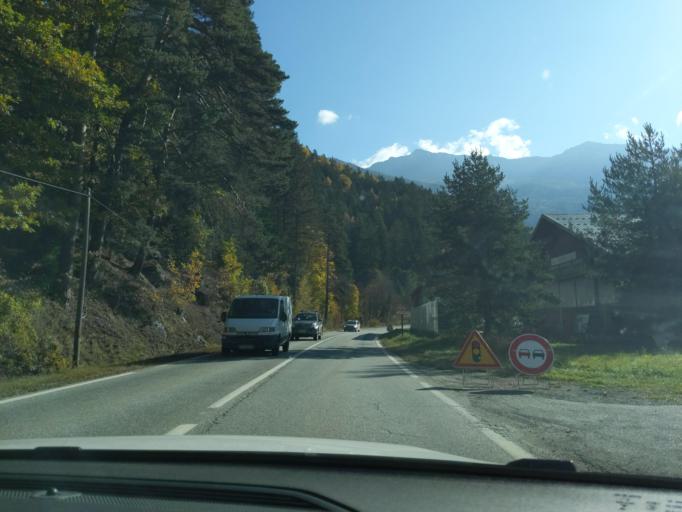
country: FR
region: Rhone-Alpes
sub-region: Departement de la Savoie
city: Seez
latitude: 45.6030
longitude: 6.8637
